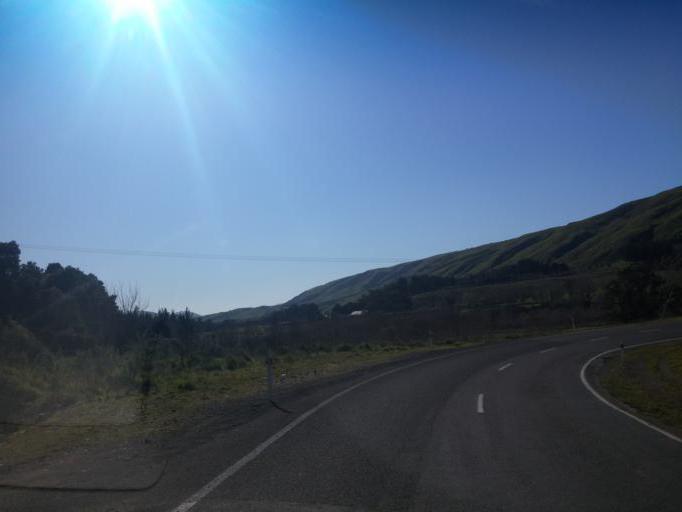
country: NZ
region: Wellington
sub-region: South Wairarapa District
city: Waipawa
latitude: -41.2949
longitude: 175.4723
